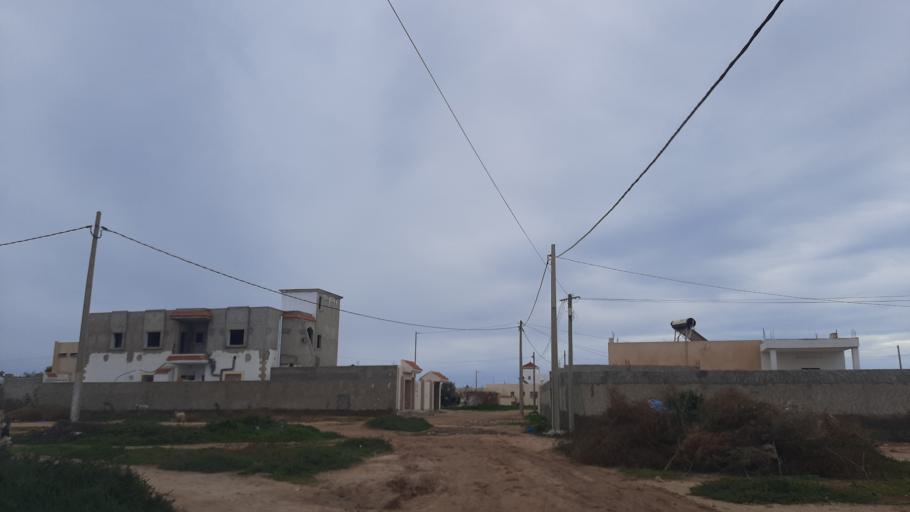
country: TN
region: Safaqis
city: Al Qarmadah
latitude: 34.7993
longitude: 10.8536
